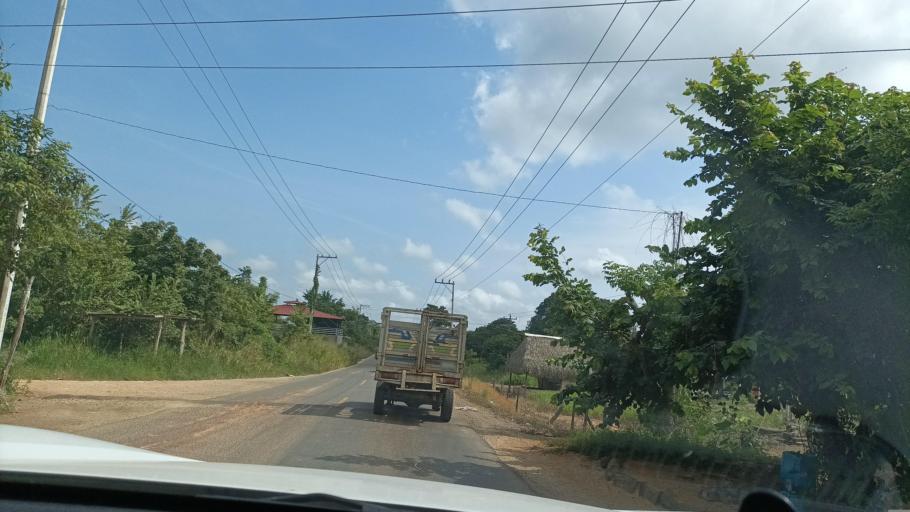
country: MX
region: Veracruz
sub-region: Chinameca
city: Chacalapa
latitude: 18.0710
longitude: -94.6872
